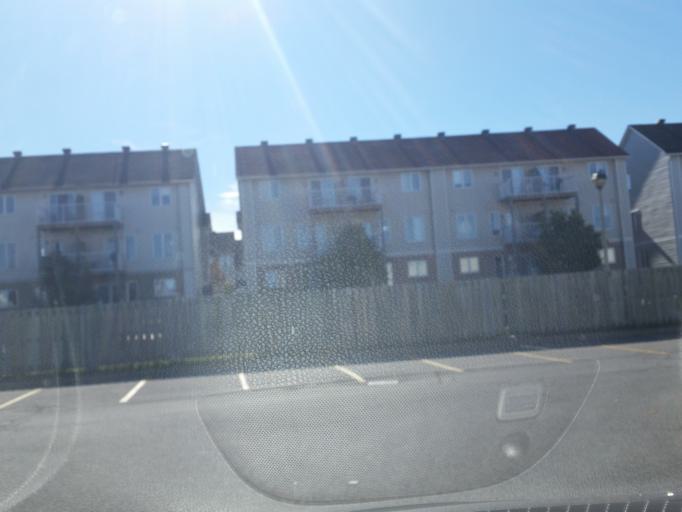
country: CA
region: Ontario
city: Ottawa
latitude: 45.4316
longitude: -75.6164
